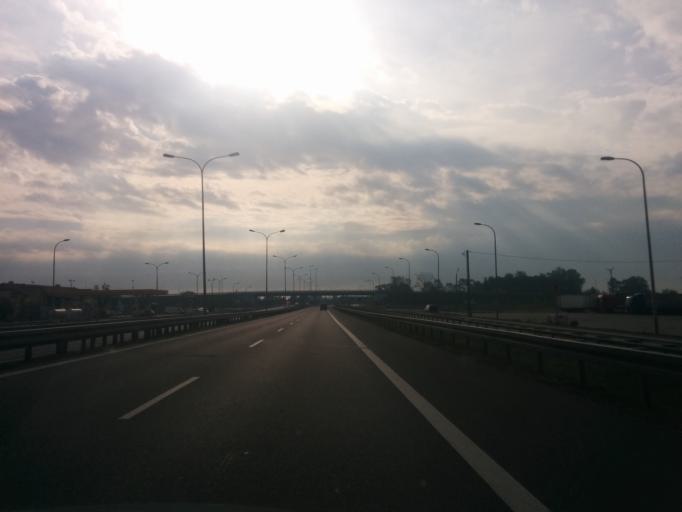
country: PL
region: Masovian Voivodeship
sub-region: Powiat bialobrzeski
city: Stara Blotnica
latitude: 51.5711
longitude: 21.0186
